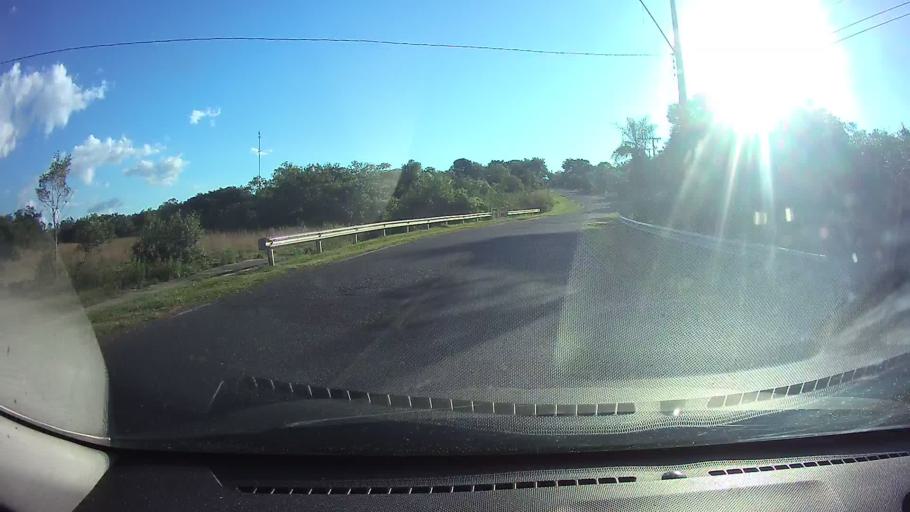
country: PY
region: Cordillera
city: Emboscada
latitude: -25.1855
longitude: -57.2998
